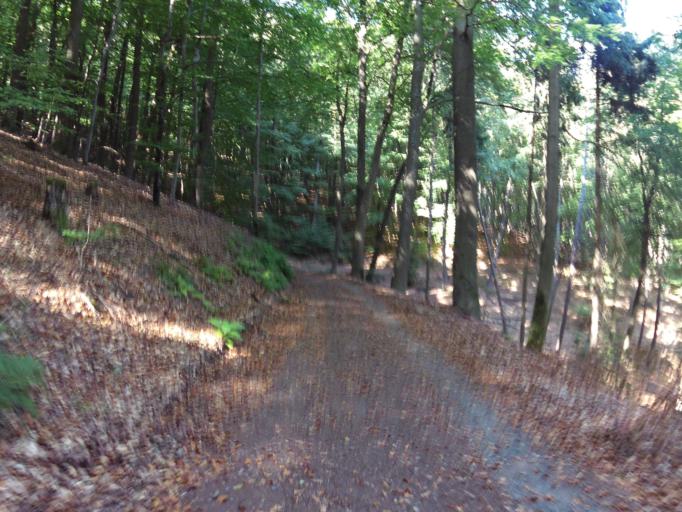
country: DE
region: Rheinland-Pfalz
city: Neidenfels
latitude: 49.4177
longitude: 8.0574
